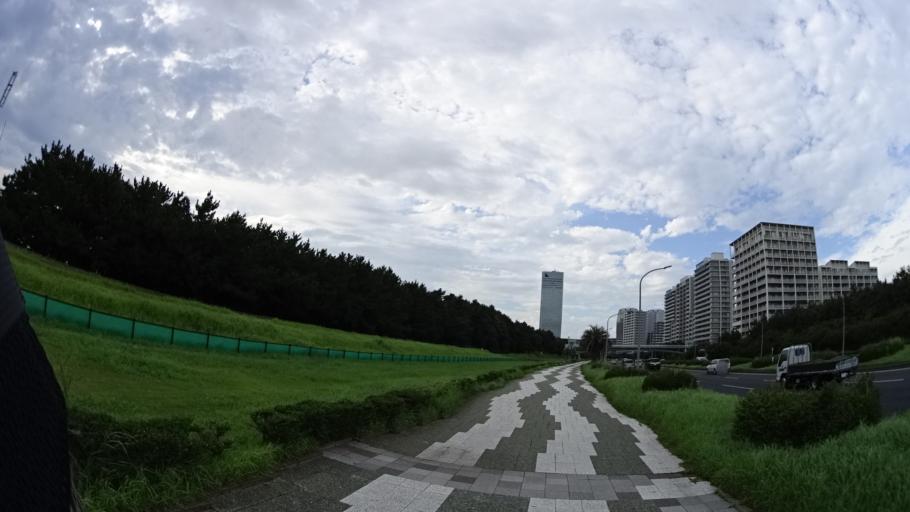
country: JP
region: Chiba
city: Funabashi
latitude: 35.6366
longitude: 140.0400
